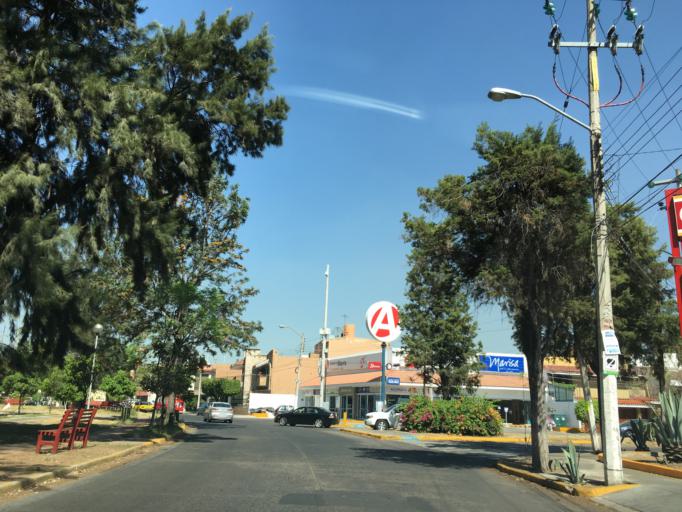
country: MX
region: Jalisco
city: Guadalajara
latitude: 20.6476
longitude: -103.3895
